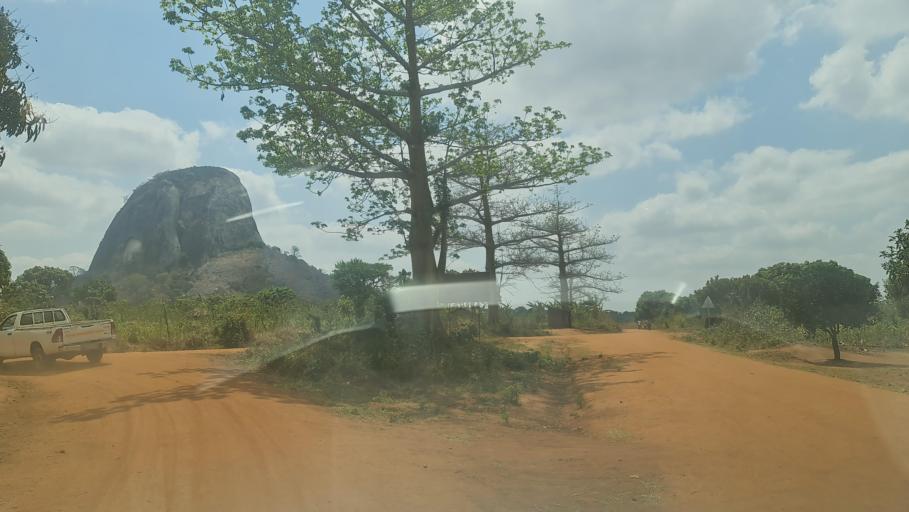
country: MW
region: Southern Region
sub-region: Nsanje District
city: Nsanje
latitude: -17.3953
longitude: 35.5725
